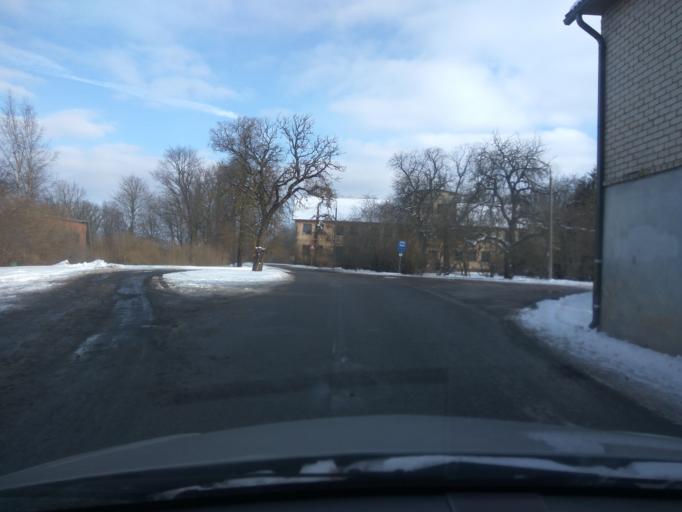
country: LV
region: Ventspils
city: Ventspils
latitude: 57.3326
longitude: 21.6421
